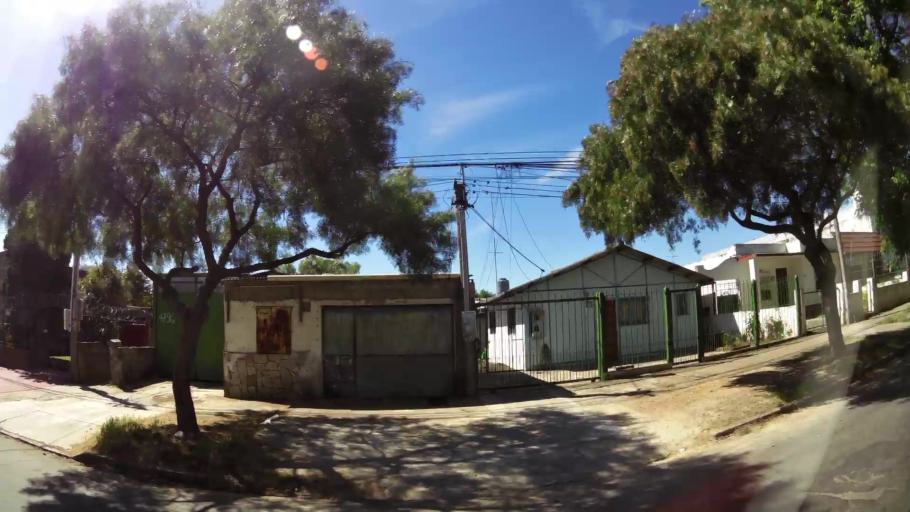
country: UY
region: Canelones
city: Paso de Carrasco
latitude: -34.8661
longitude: -56.1193
